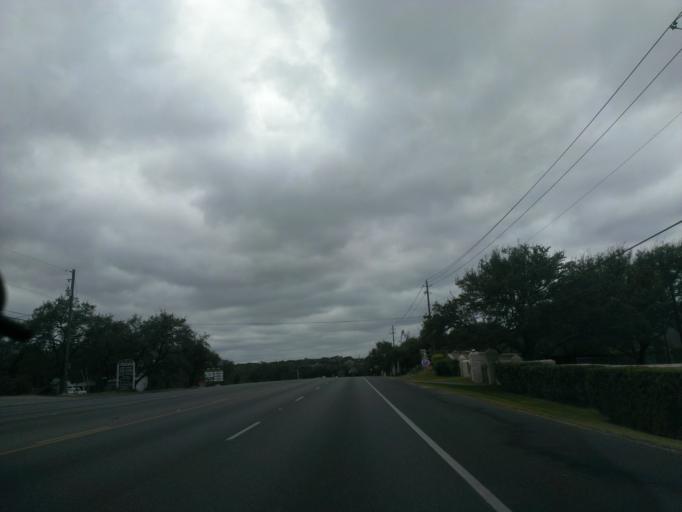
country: US
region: Texas
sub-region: Travis County
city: Hudson Bend
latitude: 30.3916
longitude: -97.9376
